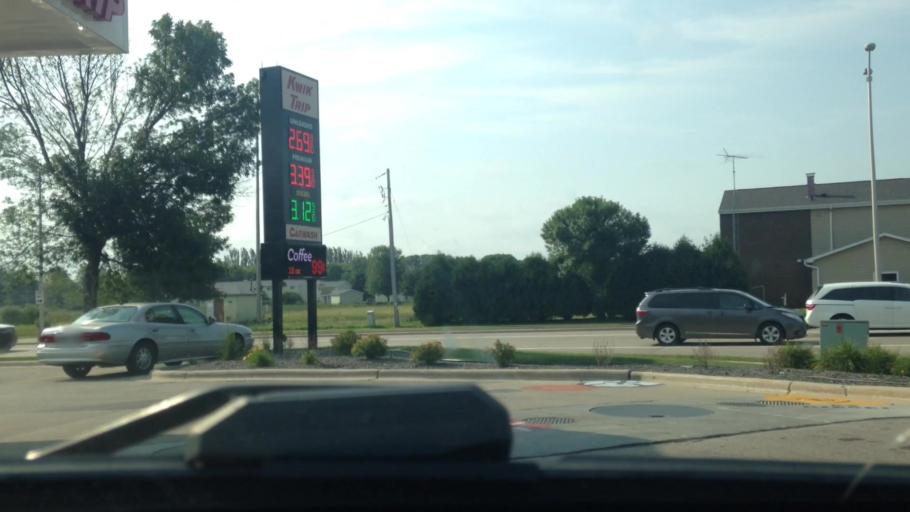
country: US
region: Wisconsin
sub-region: Fond du Lac County
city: North Fond du Lac
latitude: 43.7921
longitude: -88.4729
